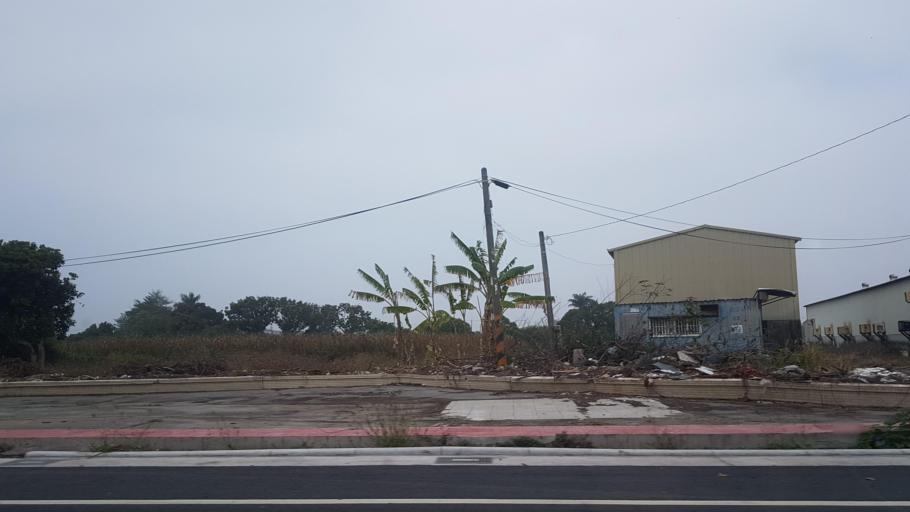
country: TW
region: Taiwan
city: Xinying
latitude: 23.3191
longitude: 120.3072
